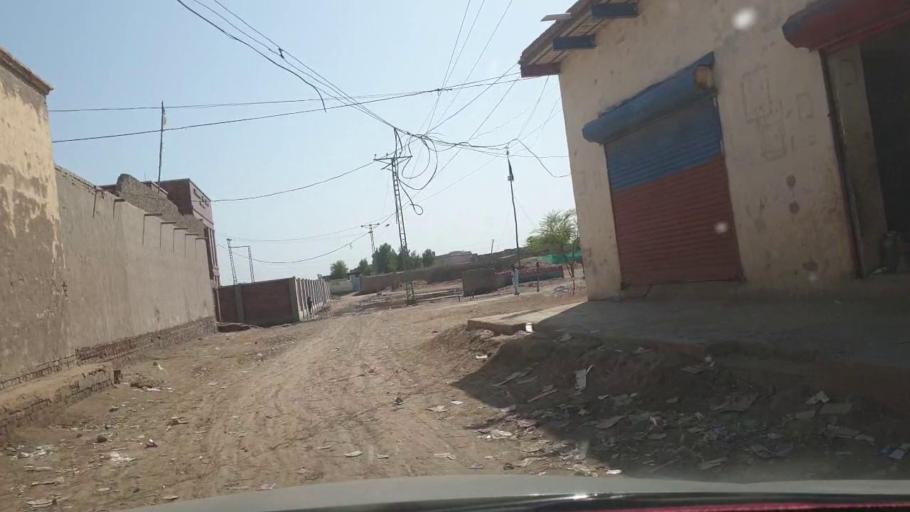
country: PK
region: Sindh
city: Nasirabad
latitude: 27.3453
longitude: 67.8403
